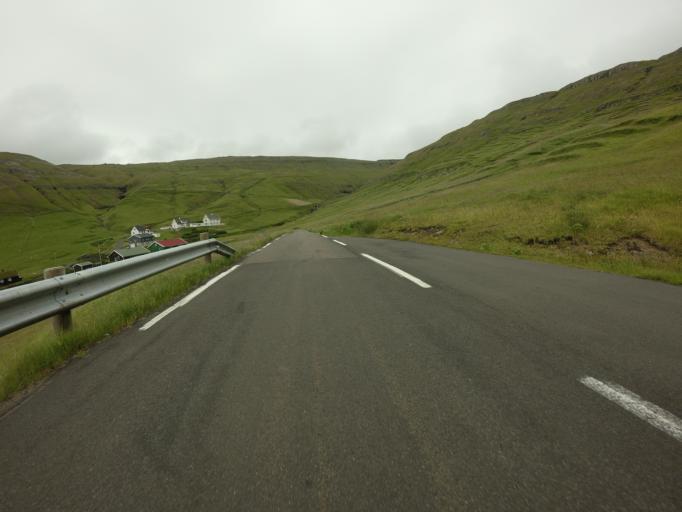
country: FO
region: Sandoy
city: Sandur
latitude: 61.7856
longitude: -6.6784
